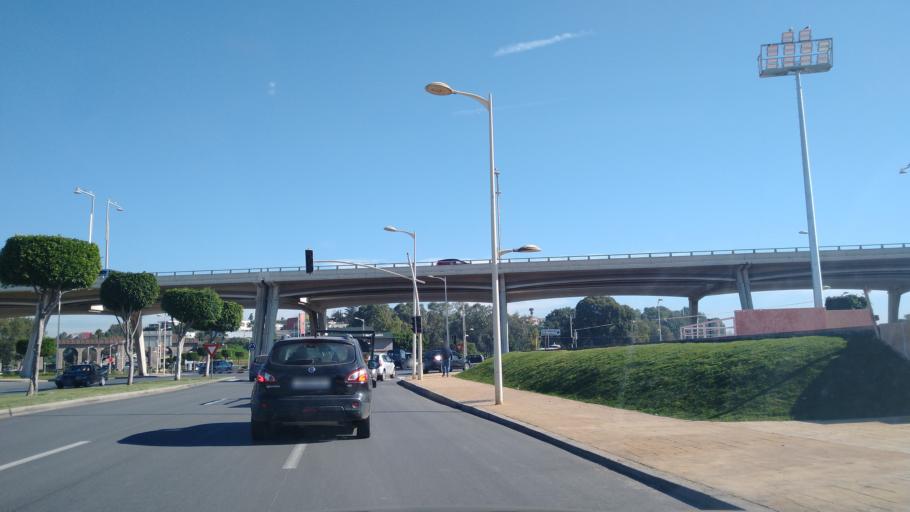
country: MA
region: Rabat-Sale-Zemmour-Zaer
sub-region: Rabat
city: Rabat
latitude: 34.0316
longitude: -6.8191
